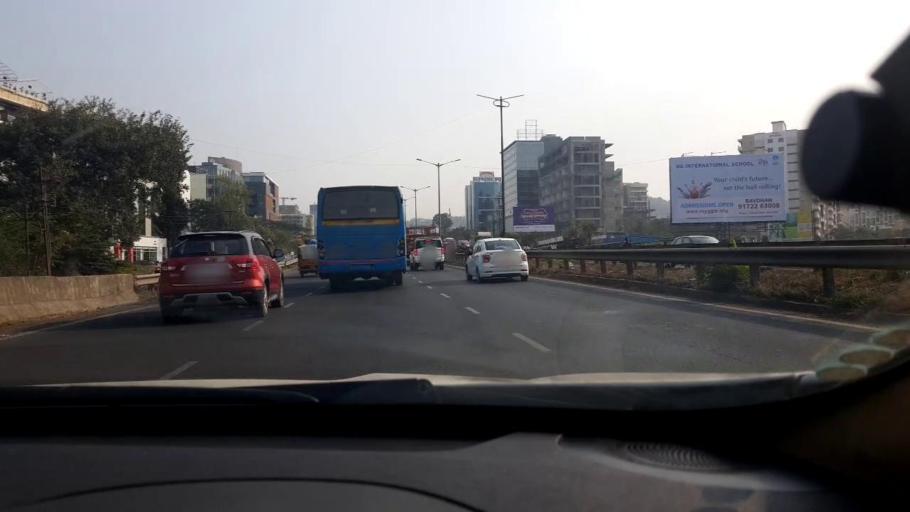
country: IN
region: Maharashtra
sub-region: Pune Division
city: Pimpri
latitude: 18.5563
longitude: 73.7705
